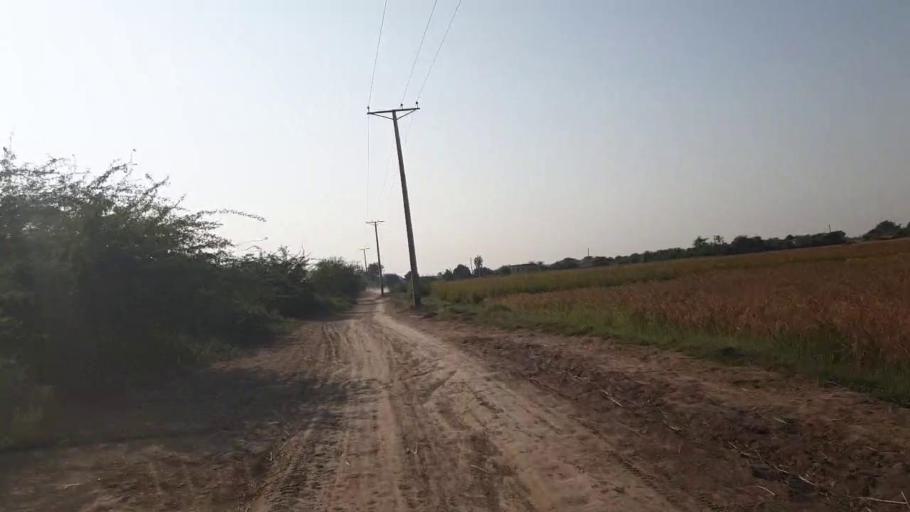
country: PK
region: Sindh
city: Kario
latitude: 24.8909
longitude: 68.6232
